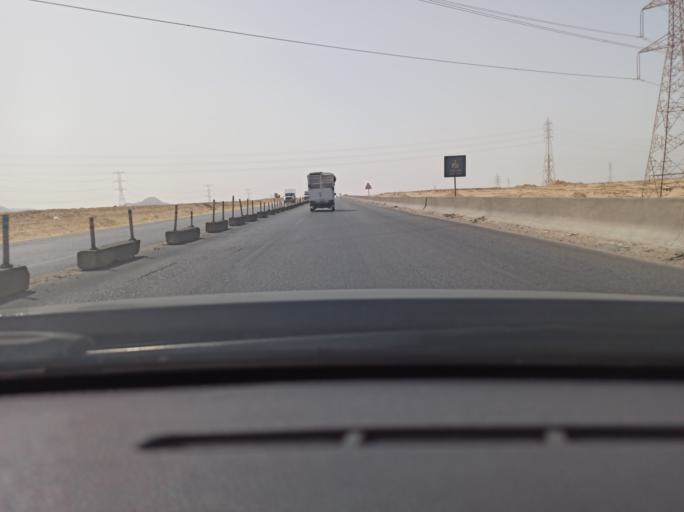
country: EG
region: Muhafazat Bani Suwayf
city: Bush
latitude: 29.1481
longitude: 31.2319
